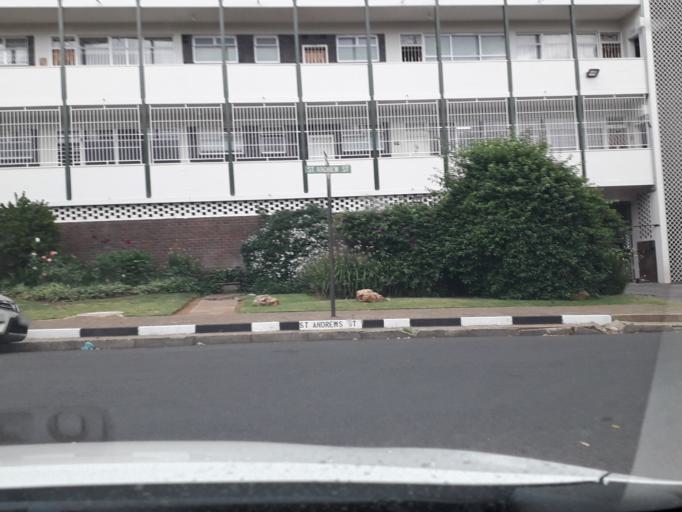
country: ZA
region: Gauteng
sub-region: City of Johannesburg Metropolitan Municipality
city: Johannesburg
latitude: -26.1376
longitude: 28.0542
